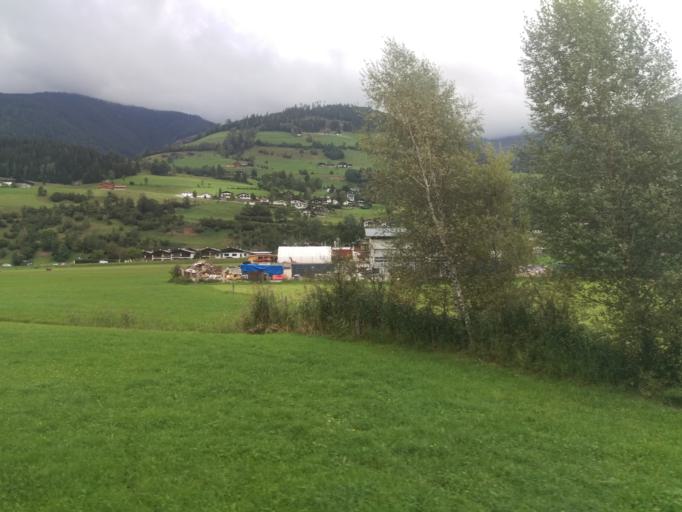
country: AT
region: Salzburg
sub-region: Politischer Bezirk Zell am See
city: Niedernsill
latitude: 47.2814
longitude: 12.6412
